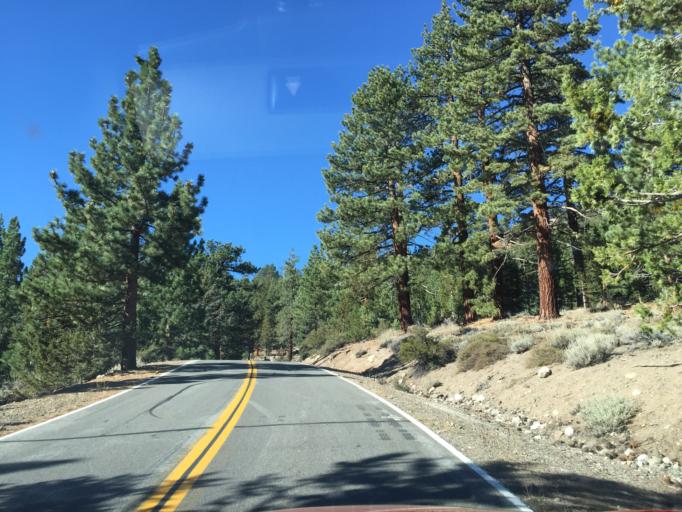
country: US
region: California
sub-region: Mono County
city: Bridgeport
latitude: 38.3265
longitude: -119.5586
